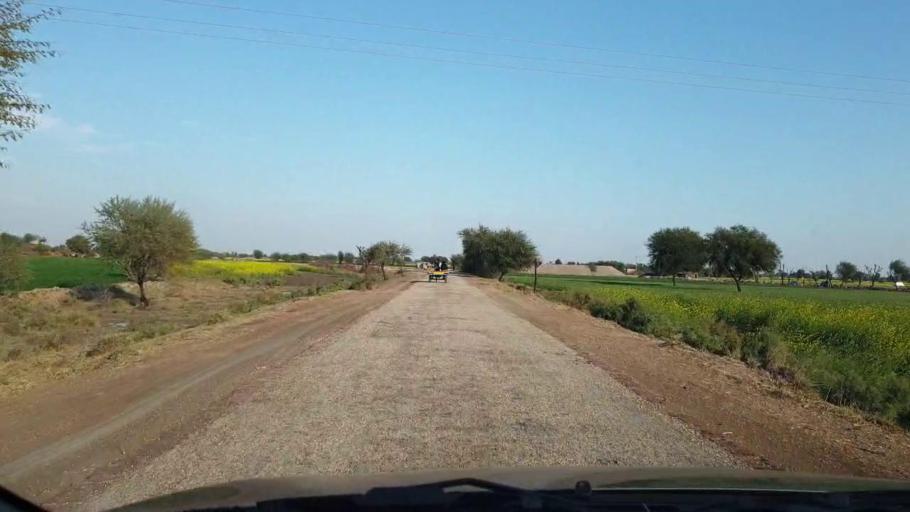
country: PK
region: Sindh
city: Jhol
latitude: 25.9623
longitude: 68.8588
